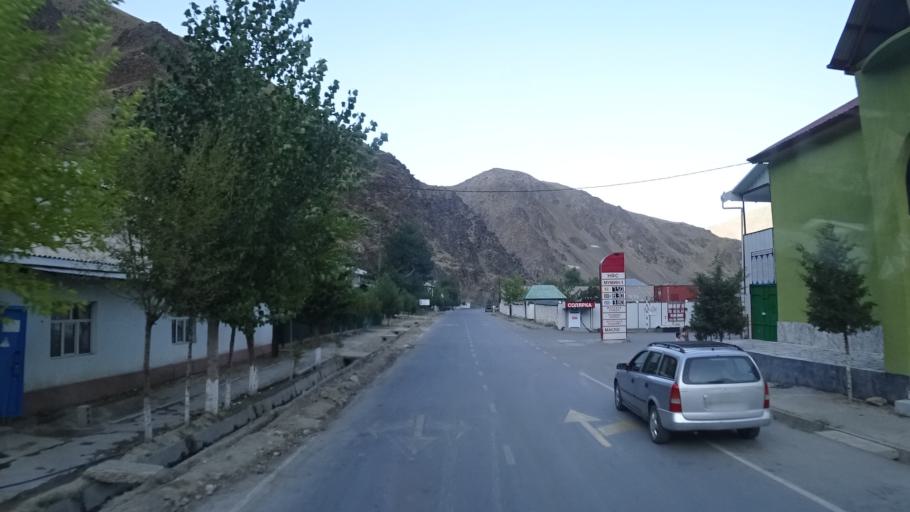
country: TJ
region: Gorno-Badakhshan
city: Qalaikhumb
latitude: 38.4566
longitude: 70.7793
